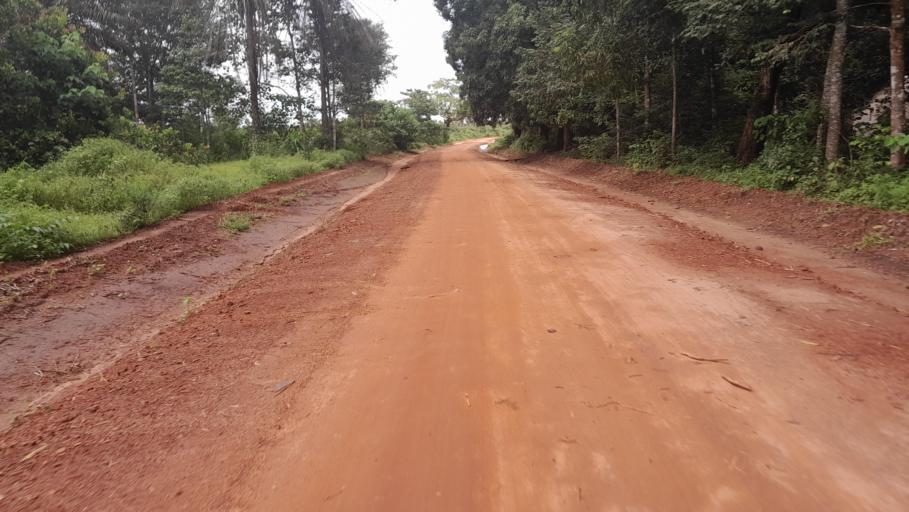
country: GN
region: Boke
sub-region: Boffa
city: Boffa
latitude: 10.0429
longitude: -13.8735
